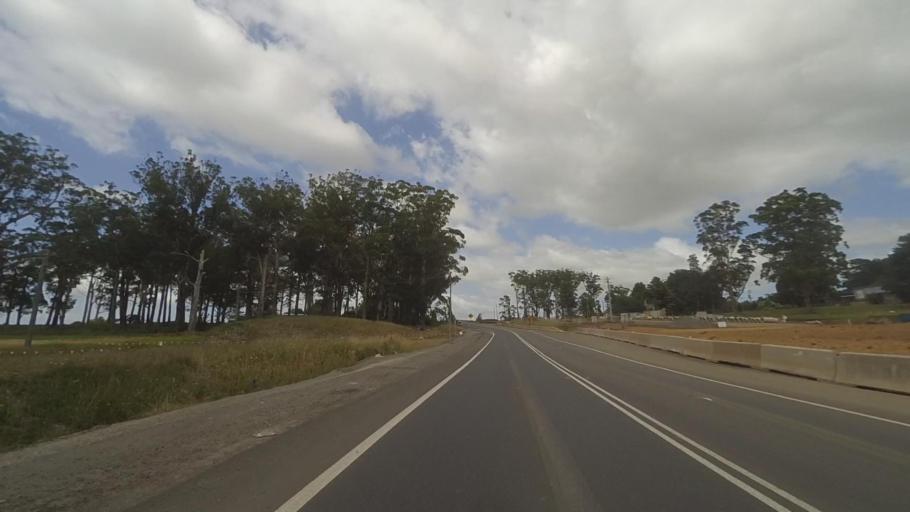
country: AU
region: New South Wales
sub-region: Shoalhaven Shire
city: Berry
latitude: -34.7815
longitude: 150.6799
